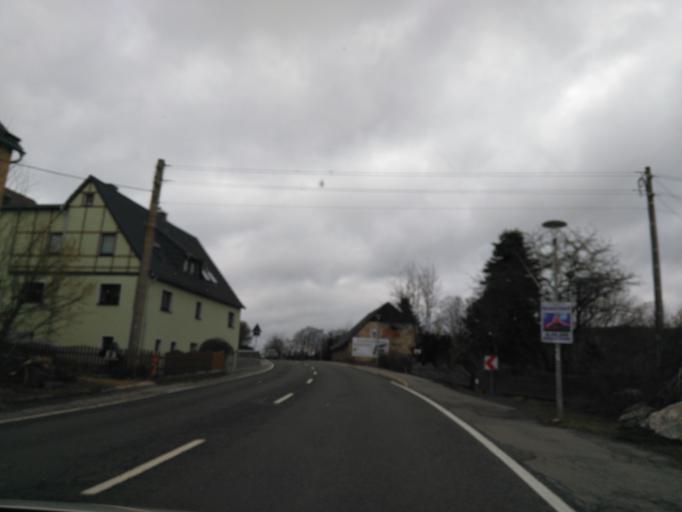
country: DE
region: Saxony
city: Ehrenfriedersdorf
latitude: 50.6214
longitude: 12.9797
